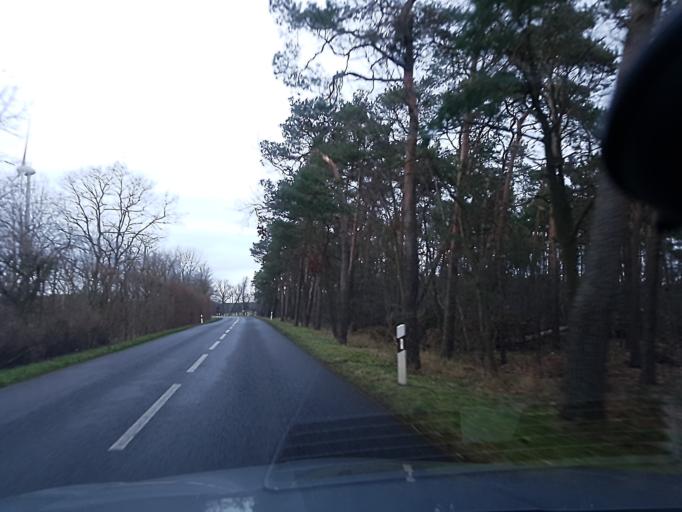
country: DE
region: Brandenburg
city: Bad Liebenwerda
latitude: 51.5396
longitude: 13.3137
